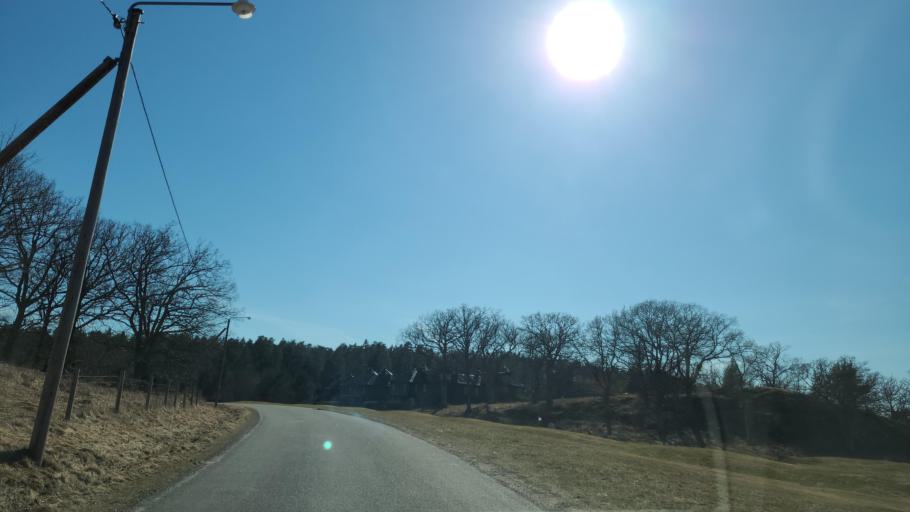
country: SE
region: Stockholm
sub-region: Varmdo Kommun
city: Hemmesta
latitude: 59.2766
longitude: 18.5481
